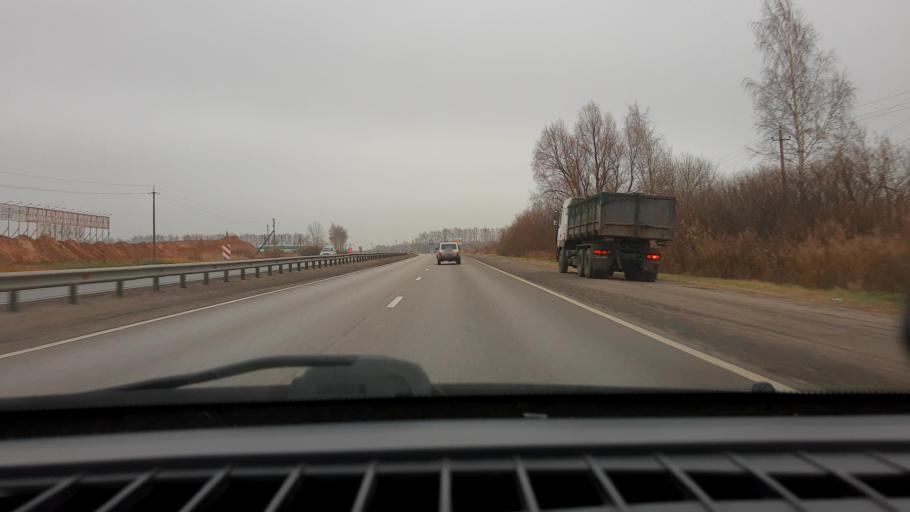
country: RU
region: Nizjnij Novgorod
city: Afonino
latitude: 56.1986
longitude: 44.1037
